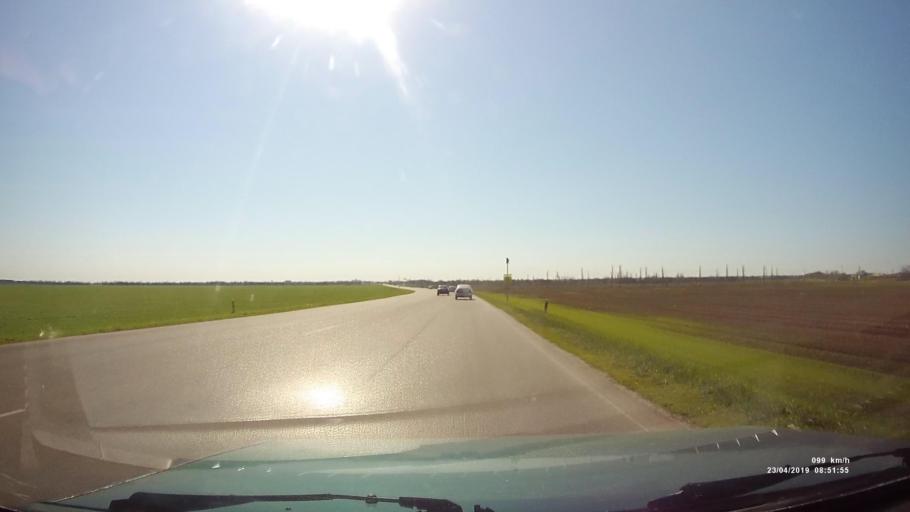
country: RU
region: Rostov
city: Sal'sk
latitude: 46.4849
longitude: 41.4503
